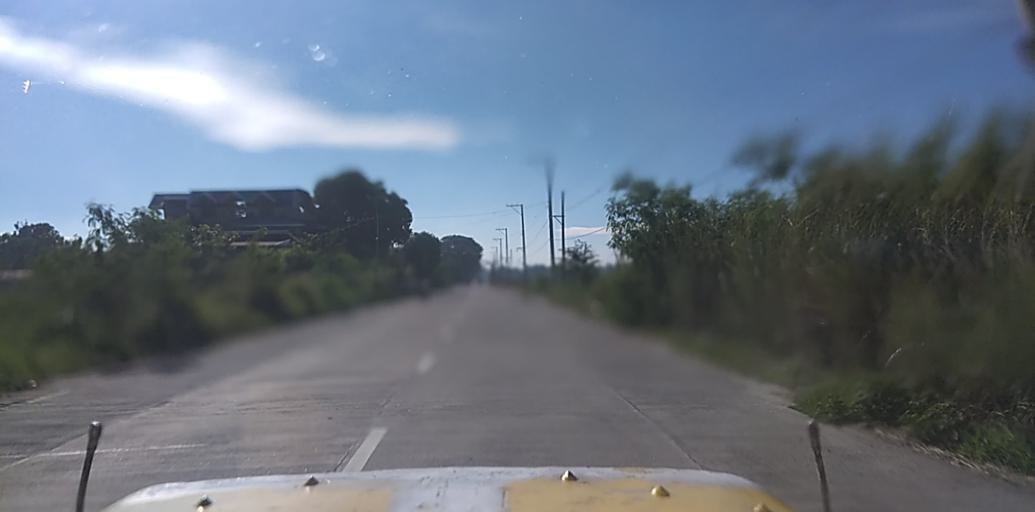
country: PH
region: Central Luzon
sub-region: Province of Pampanga
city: Anao
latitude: 15.1323
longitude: 120.6969
